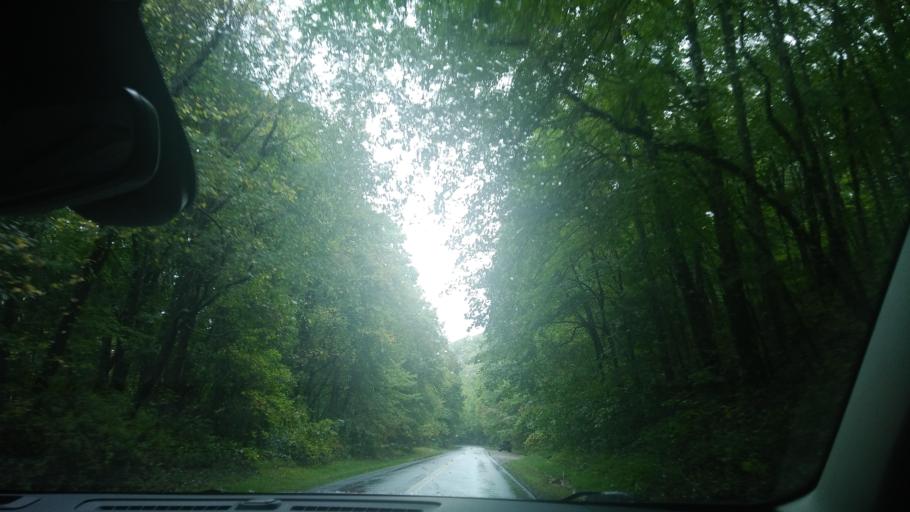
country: US
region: North Carolina
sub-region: Buncombe County
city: Biltmore Forest
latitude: 35.5324
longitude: -82.5081
